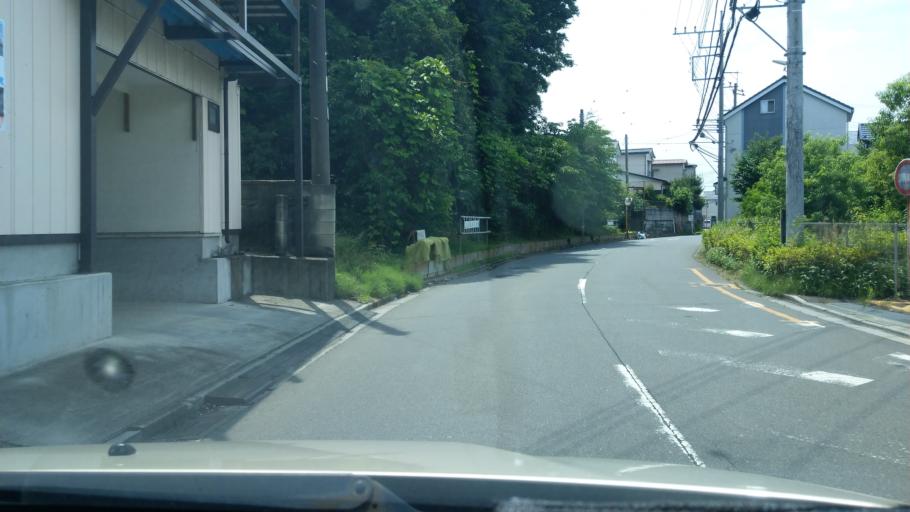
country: JP
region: Saitama
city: Saitama
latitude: 35.9113
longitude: 139.6492
